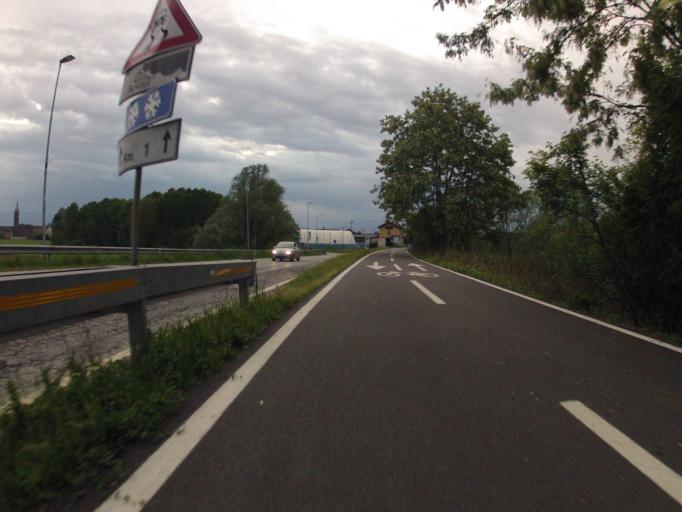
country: IT
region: Piedmont
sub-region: Provincia di Torino
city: Villafranca Piemonte
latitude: 44.7803
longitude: 7.5118
